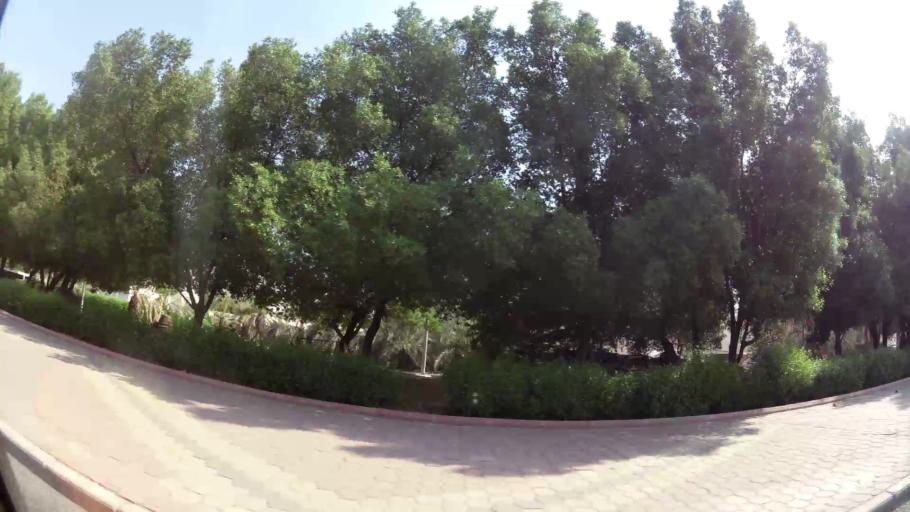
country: KW
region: Al Asimah
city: Ad Dasmah
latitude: 29.3548
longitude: 48.0173
